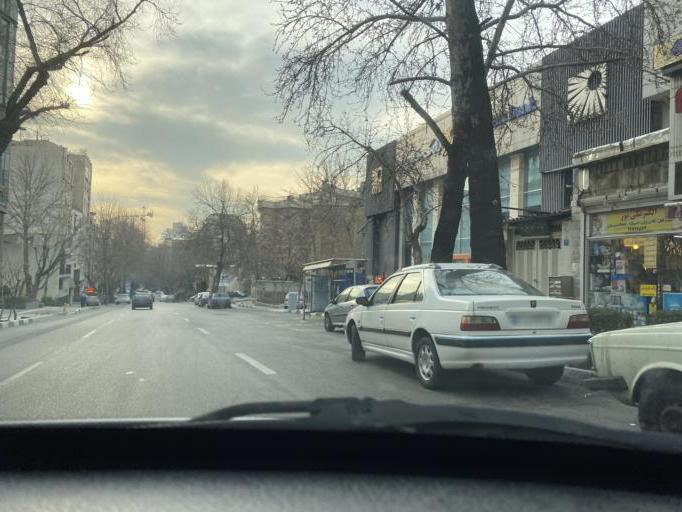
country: IR
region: Tehran
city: Tajrish
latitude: 35.8122
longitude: 51.4494
